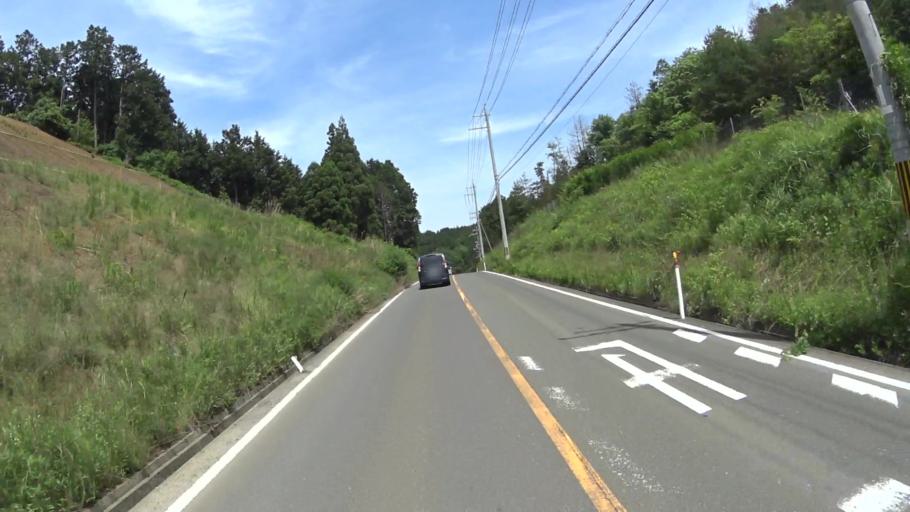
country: JP
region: Fukui
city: Obama
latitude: 35.4701
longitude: 135.6277
